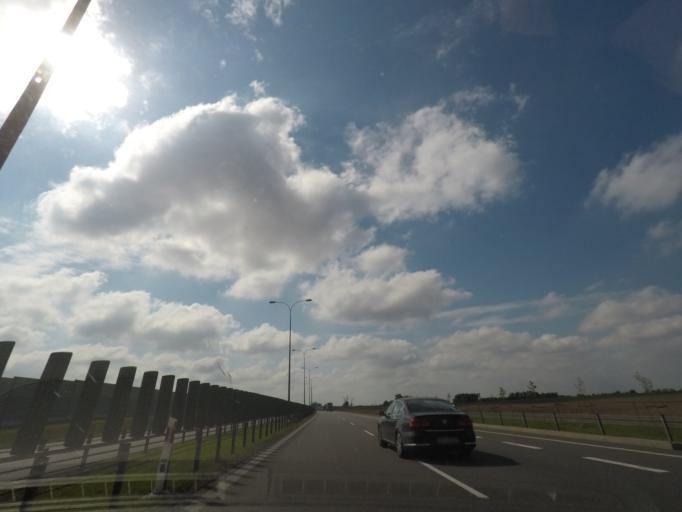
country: PL
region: Kujawsko-Pomorskie
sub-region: Powiat chelminski
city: Lisewo
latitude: 53.2837
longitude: 18.7100
